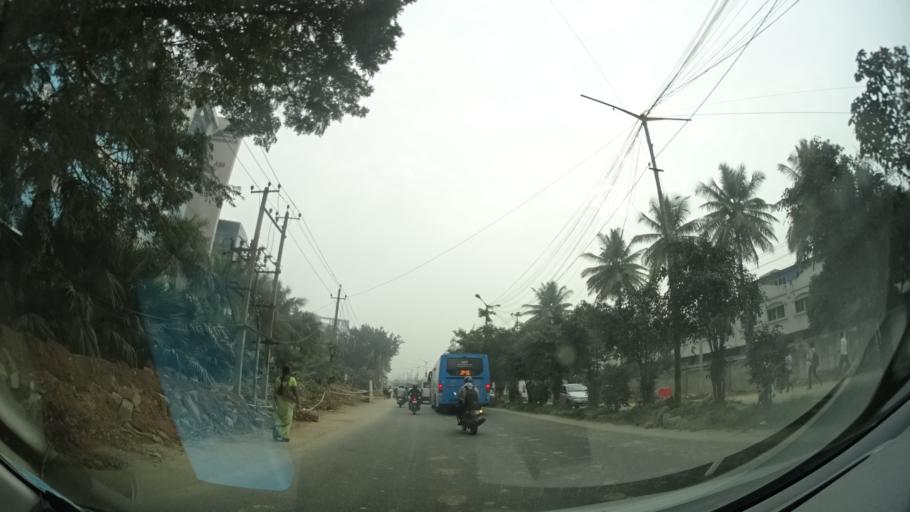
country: IN
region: Karnataka
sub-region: Bangalore Urban
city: Bangalore
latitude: 12.9932
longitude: 77.7048
